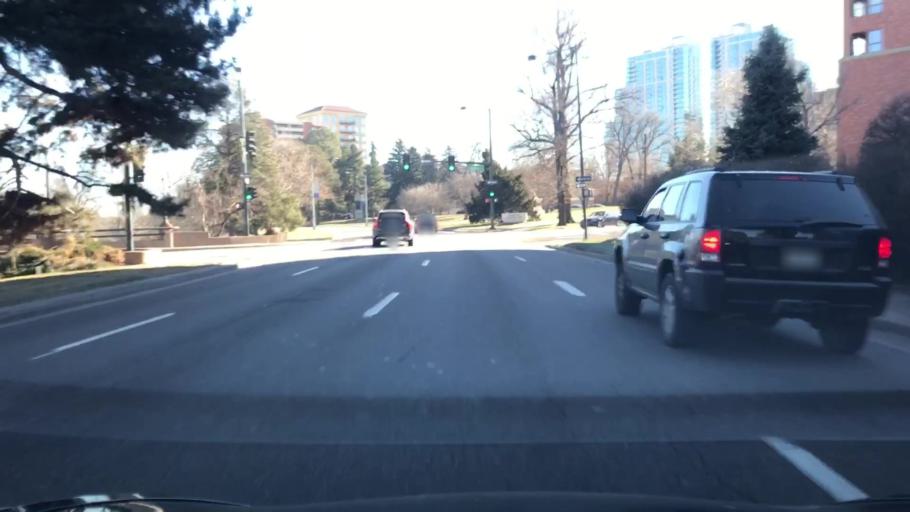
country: US
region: Colorado
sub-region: Denver County
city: Denver
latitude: 39.7197
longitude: -104.9780
